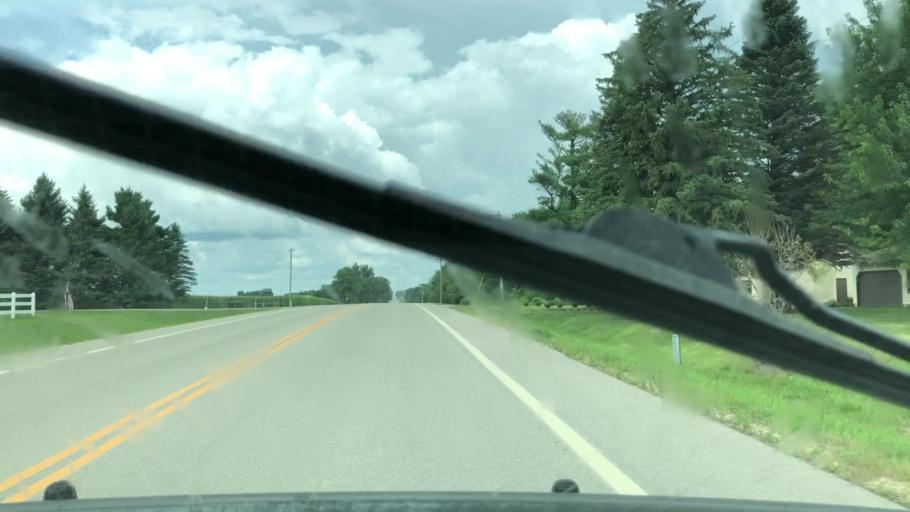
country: US
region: Minnesota
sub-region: Olmsted County
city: Stewartville
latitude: 43.8659
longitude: -92.5287
